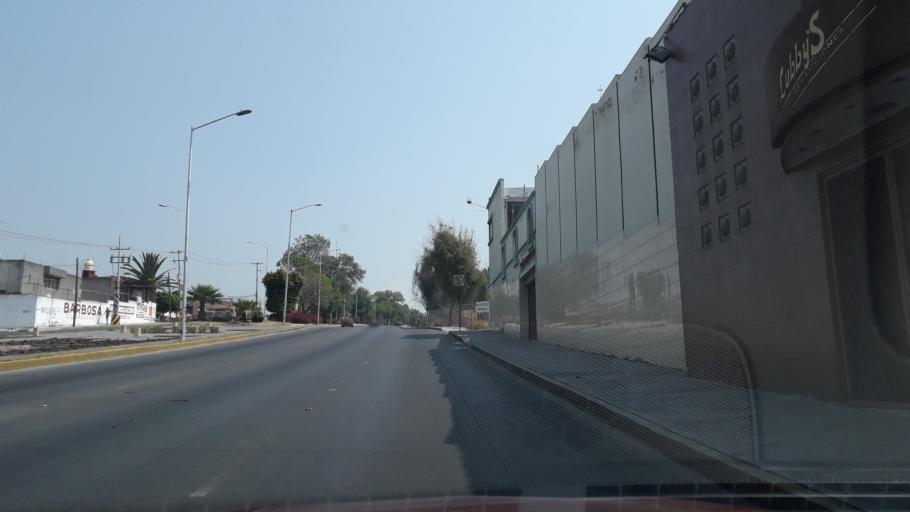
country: MX
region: Puebla
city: Puebla
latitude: 19.0549
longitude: -98.1901
